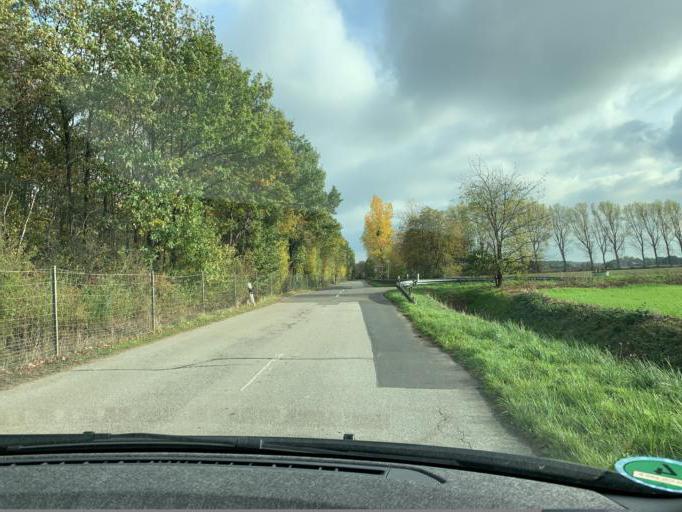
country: DE
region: North Rhine-Westphalia
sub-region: Regierungsbezirk Koln
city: Niederzier
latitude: 50.8707
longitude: 6.5050
